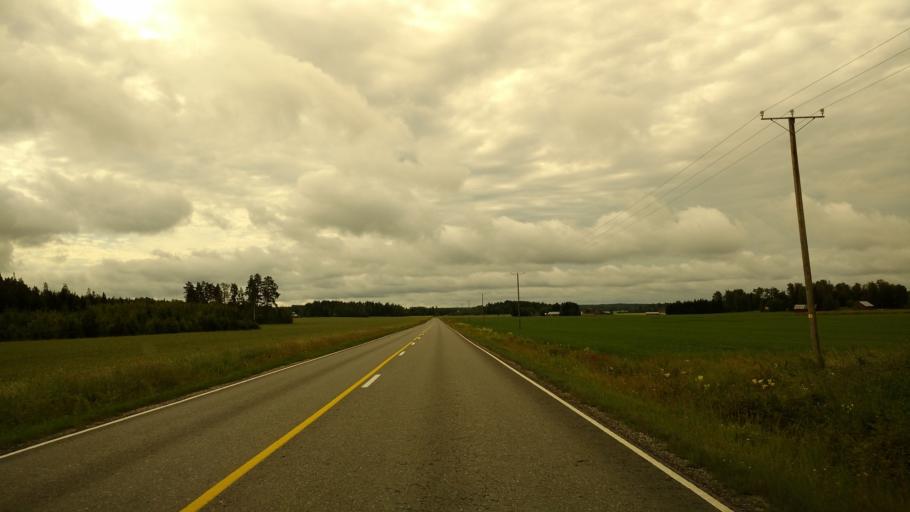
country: FI
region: Varsinais-Suomi
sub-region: Salo
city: Kuusjoki
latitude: 60.4965
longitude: 23.1649
